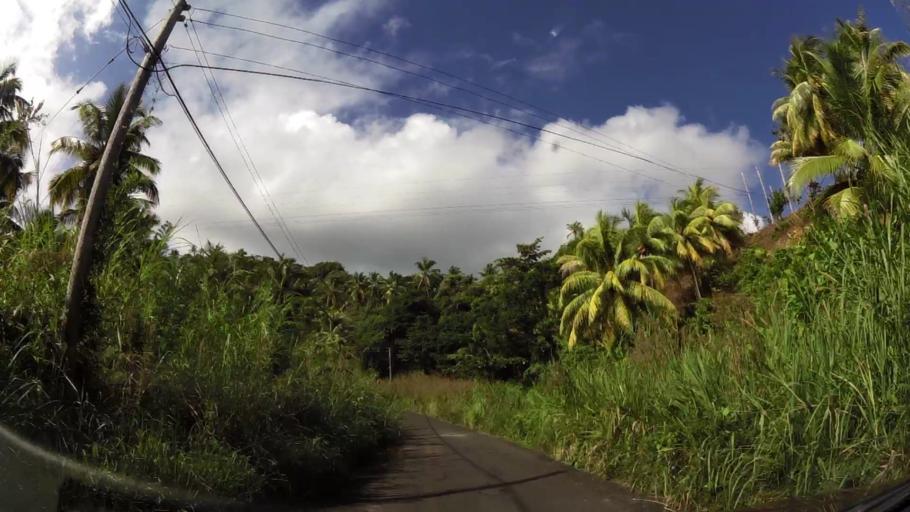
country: DM
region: Saint David
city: Castle Bruce
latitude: 15.4716
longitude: -61.2486
